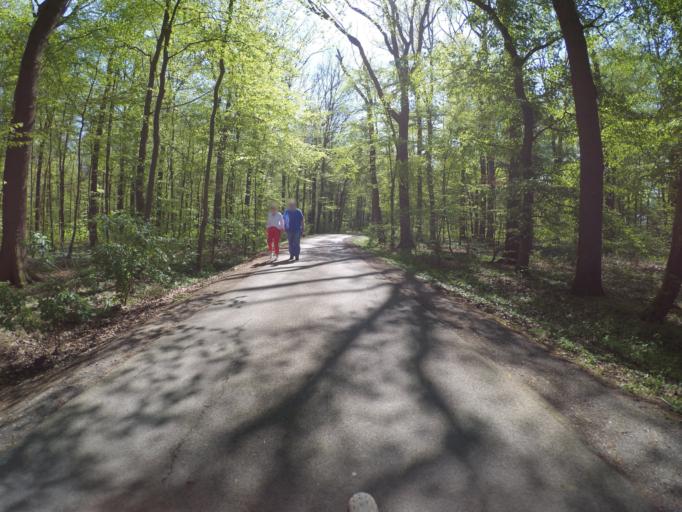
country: DE
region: North Rhine-Westphalia
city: Ludinghausen
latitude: 51.7582
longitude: 7.4405
